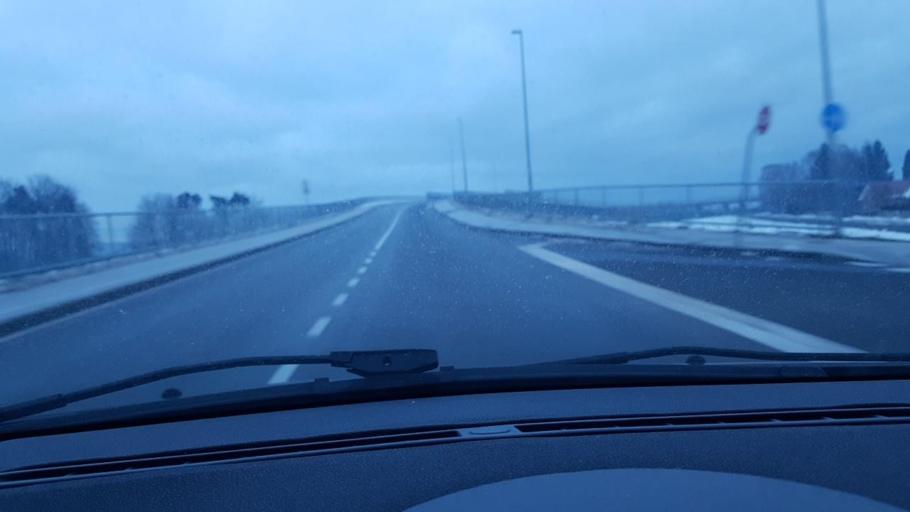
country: SI
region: Hajdina
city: Spodnja Hajdina
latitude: 46.3993
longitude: 15.8260
